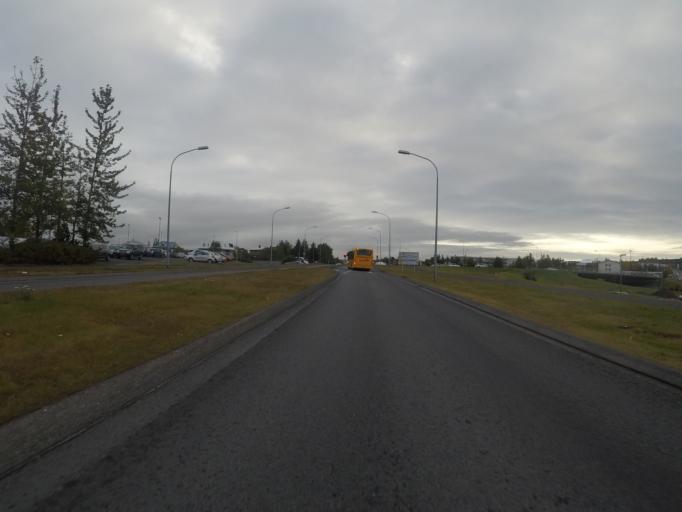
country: IS
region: Capital Region
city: Kopavogur
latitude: 64.1372
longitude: -21.9259
